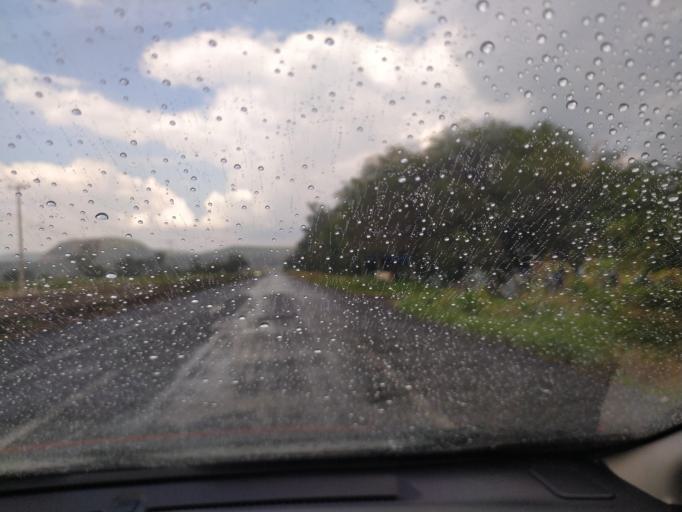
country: MX
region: Jalisco
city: Bellavista
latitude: 20.4198
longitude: -103.6174
